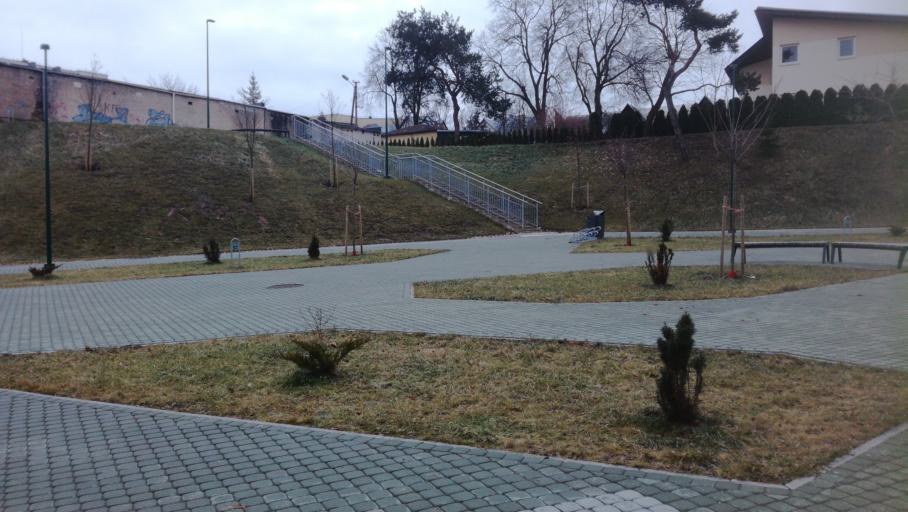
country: LT
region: Alytaus apskritis
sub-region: Alytus
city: Alytus
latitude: 54.3976
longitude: 24.0411
